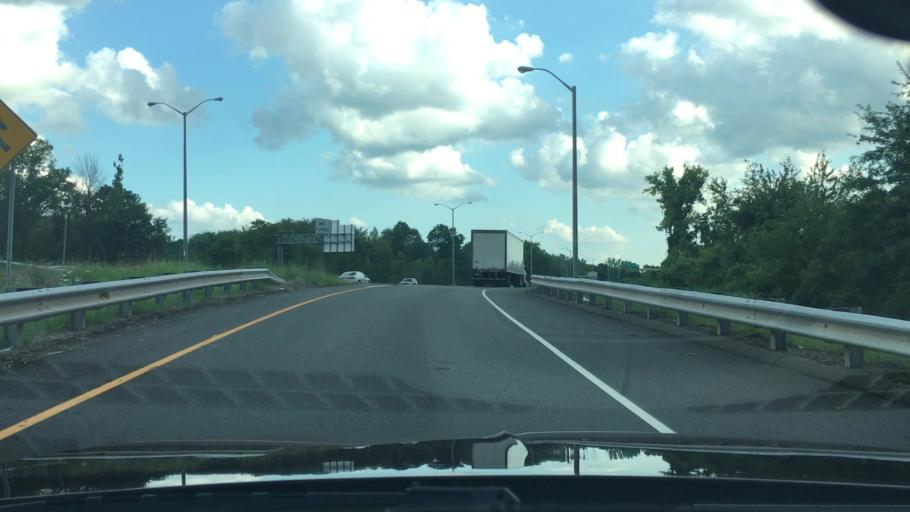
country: US
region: Connecticut
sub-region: Hartford County
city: Windsor Locks
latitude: 41.9291
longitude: -72.6094
